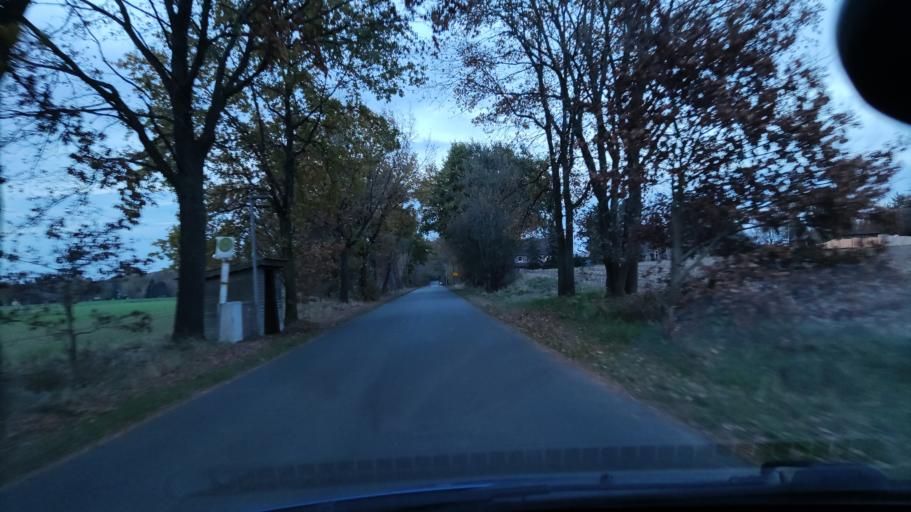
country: DE
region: Lower Saxony
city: Bispingen
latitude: 53.1374
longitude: 10.0230
